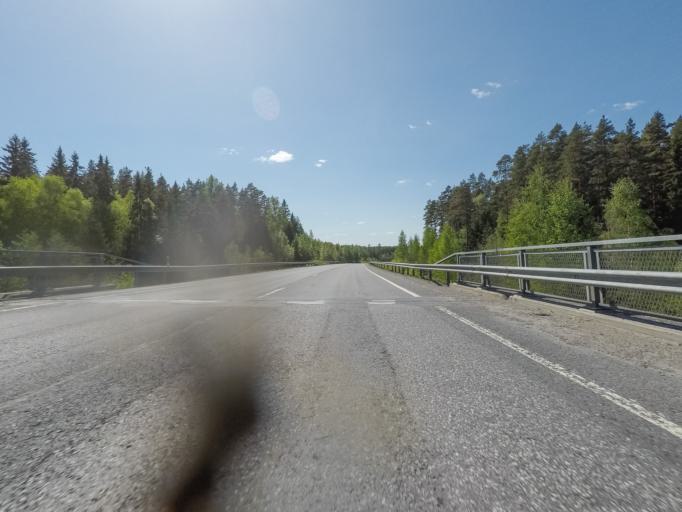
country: FI
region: Pirkanmaa
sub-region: Etelae-Pirkanmaa
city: Toijala
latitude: 61.1874
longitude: 23.8033
